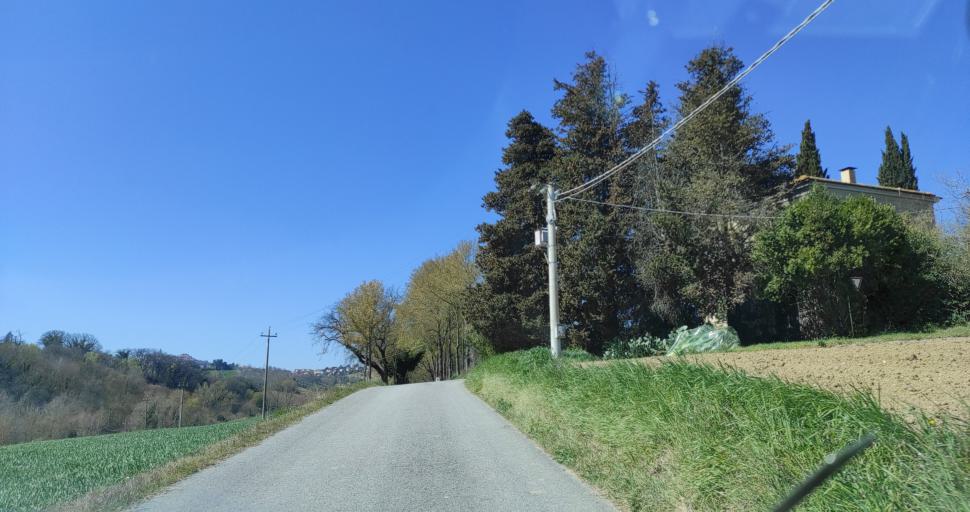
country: IT
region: The Marches
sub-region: Provincia di Macerata
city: Piediripa
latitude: 43.3125
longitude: 13.4925
